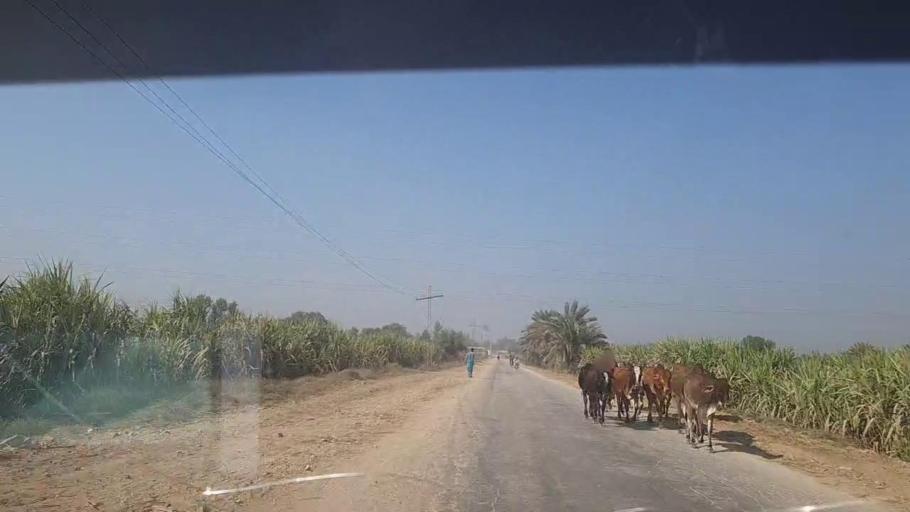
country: PK
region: Sindh
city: Kot Diji
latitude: 27.4273
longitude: 68.6554
